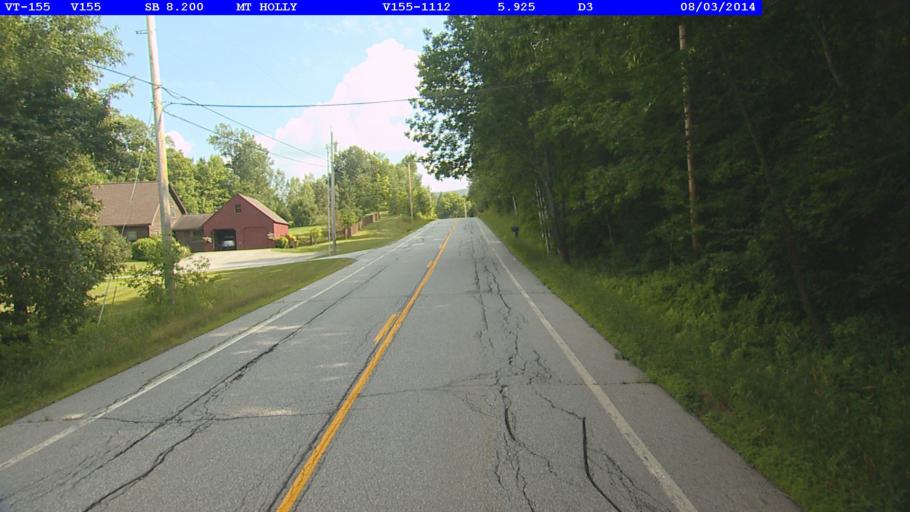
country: US
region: Vermont
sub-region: Rutland County
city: Rutland
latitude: 43.4282
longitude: -72.8576
